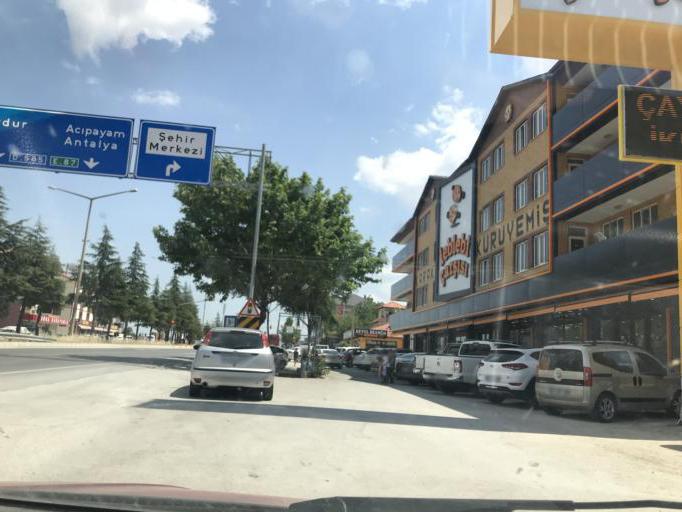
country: TR
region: Denizli
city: Serinhisar
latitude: 37.5840
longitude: 29.2696
